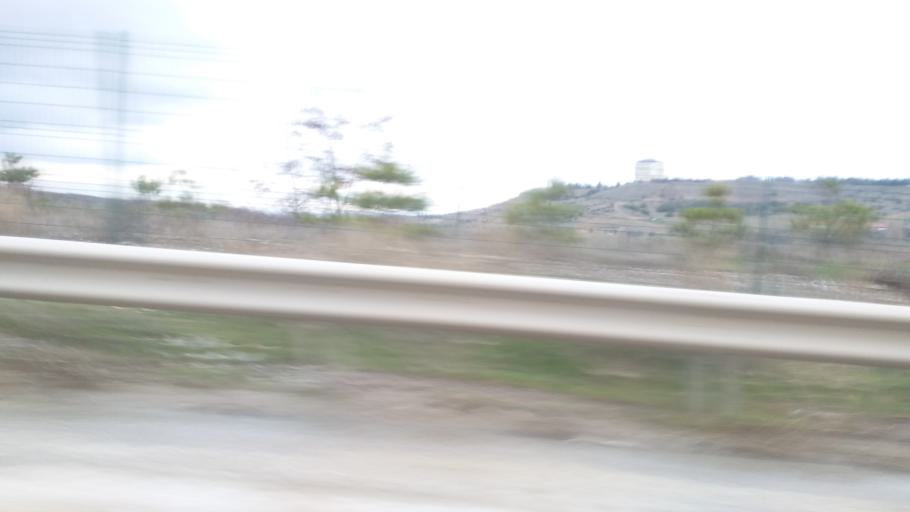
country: TR
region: Ankara
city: Ankara
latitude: 39.9208
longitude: 32.7935
